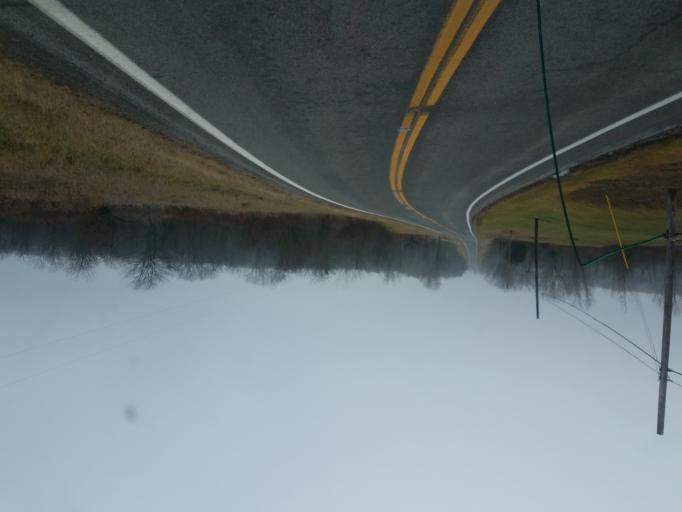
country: US
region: Ohio
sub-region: Champaign County
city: North Lewisburg
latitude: 40.3003
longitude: -83.5667
